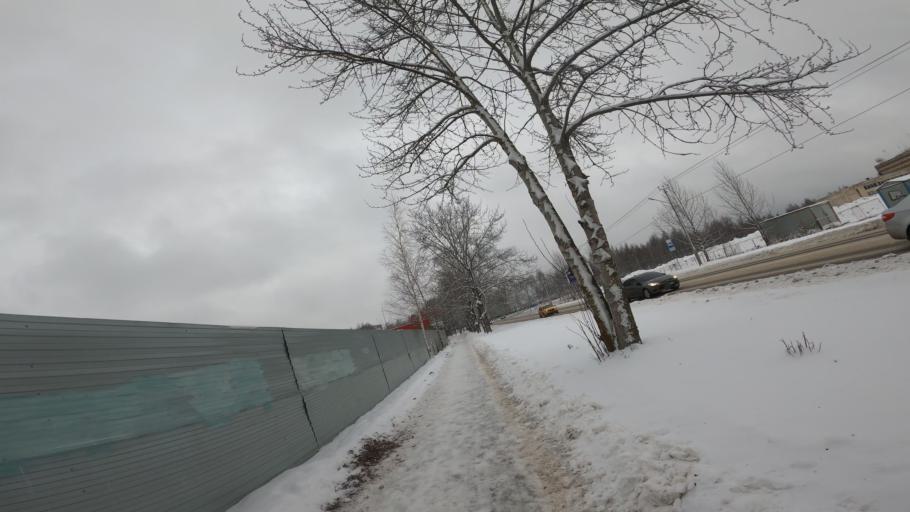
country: RU
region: Jaroslavl
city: Pereslavl'-Zalesskiy
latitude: 56.7496
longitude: 38.8861
